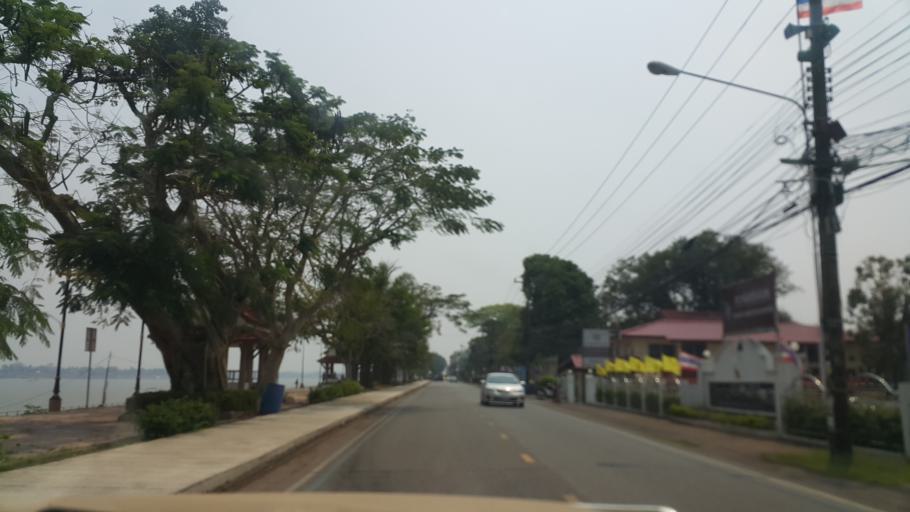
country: TH
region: Nakhon Phanom
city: Nakhon Phanom
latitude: 17.4076
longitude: 104.7857
